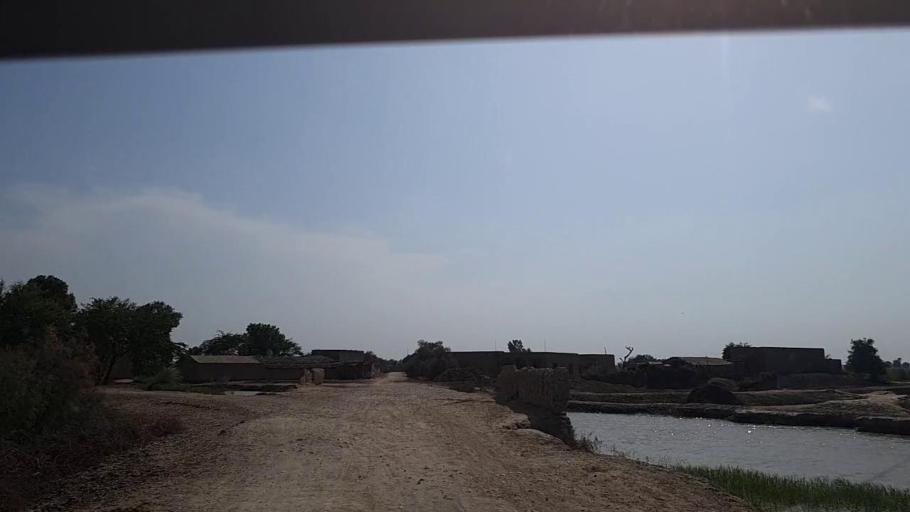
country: PK
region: Sindh
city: Khanpur
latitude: 27.8506
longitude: 69.3582
